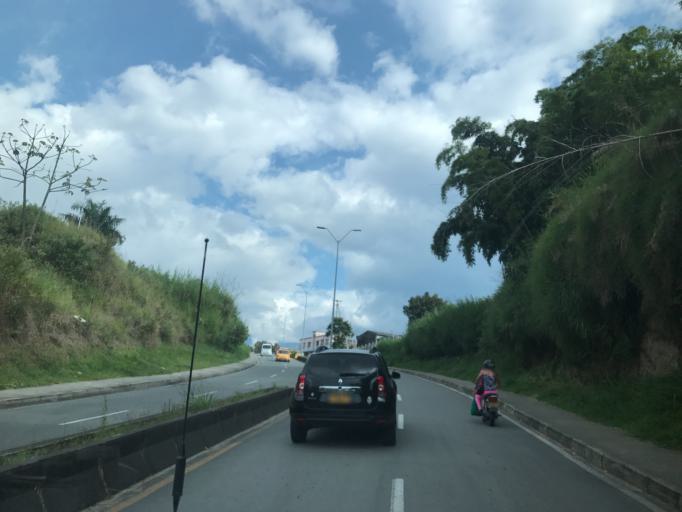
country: CO
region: Quindio
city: Armenia
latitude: 4.5376
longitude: -75.6834
